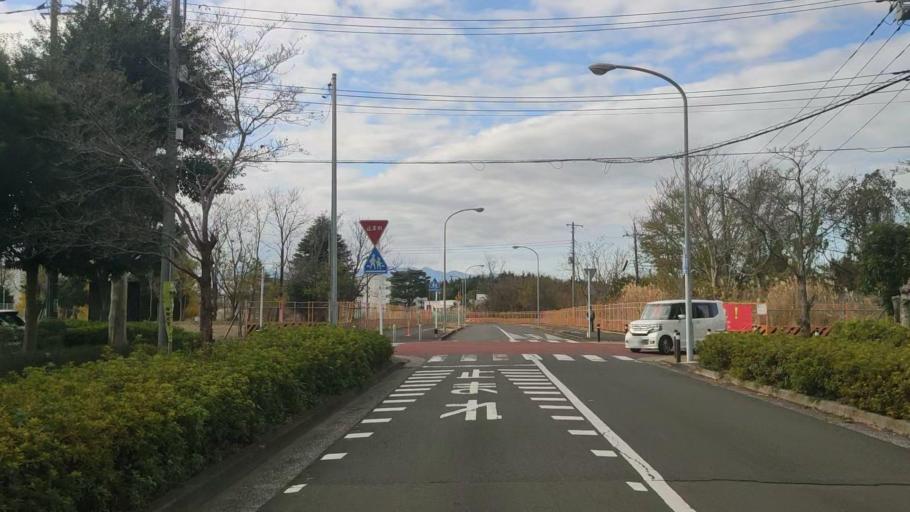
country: JP
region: Kanagawa
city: Minami-rinkan
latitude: 35.4831
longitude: 139.4893
